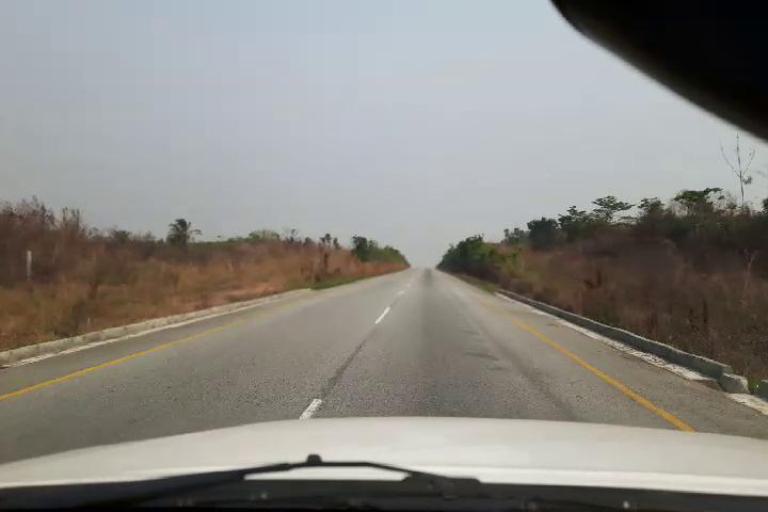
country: SL
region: Southern Province
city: Largo
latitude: 8.2305
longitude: -12.0793
